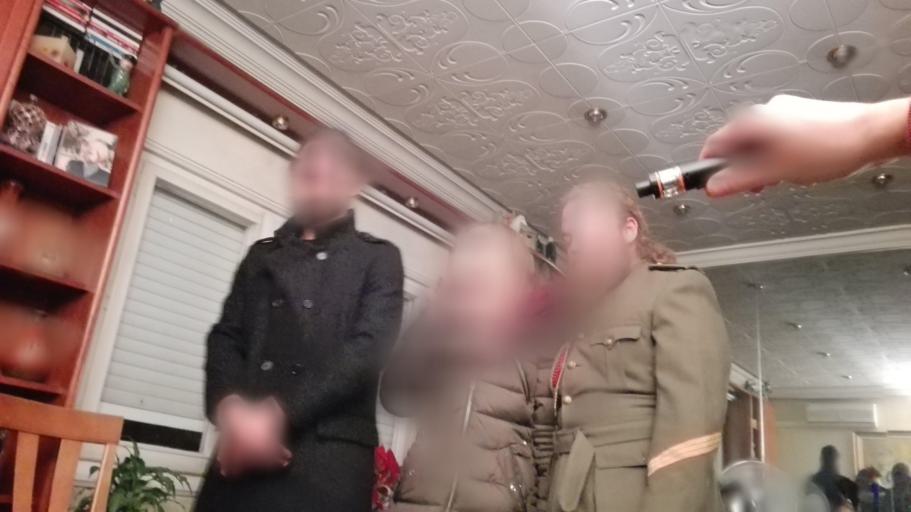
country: ES
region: Madrid
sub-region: Provincia de Madrid
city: Retiro
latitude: 40.4050
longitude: -3.6772
